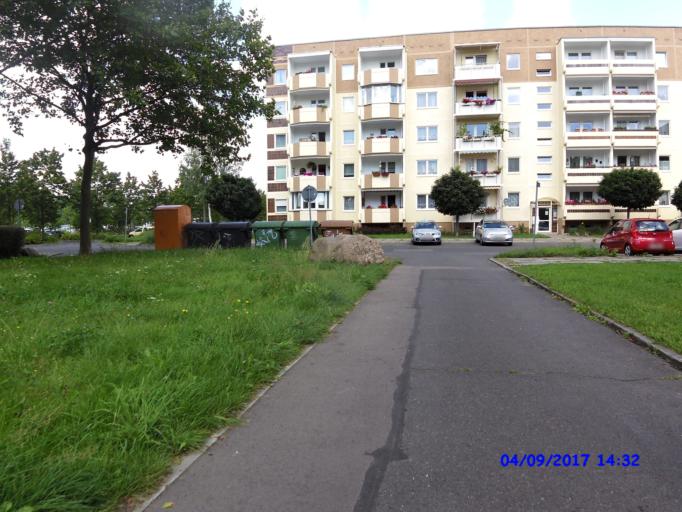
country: DE
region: Saxony
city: Taucha
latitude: 51.3568
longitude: 12.4634
